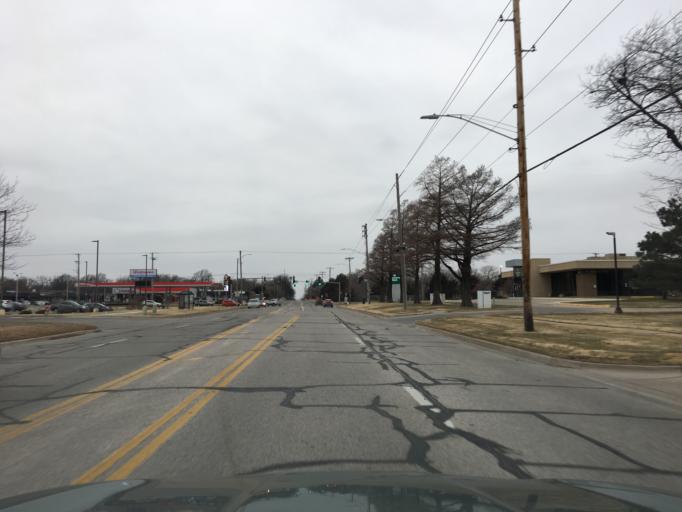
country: US
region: Kansas
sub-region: Sedgwick County
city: Bellaire
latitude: 37.7084
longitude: -97.2604
